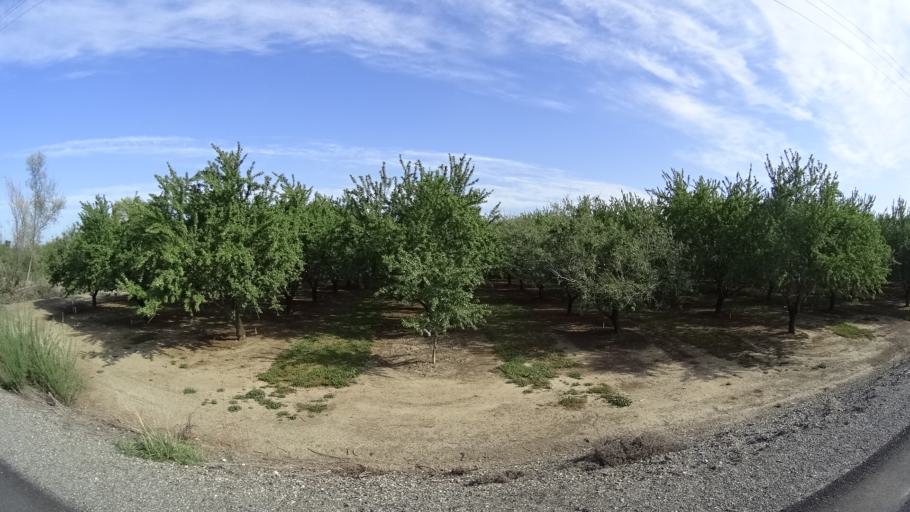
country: US
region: California
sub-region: Glenn County
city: Hamilton City
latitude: 39.6306
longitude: -122.0016
